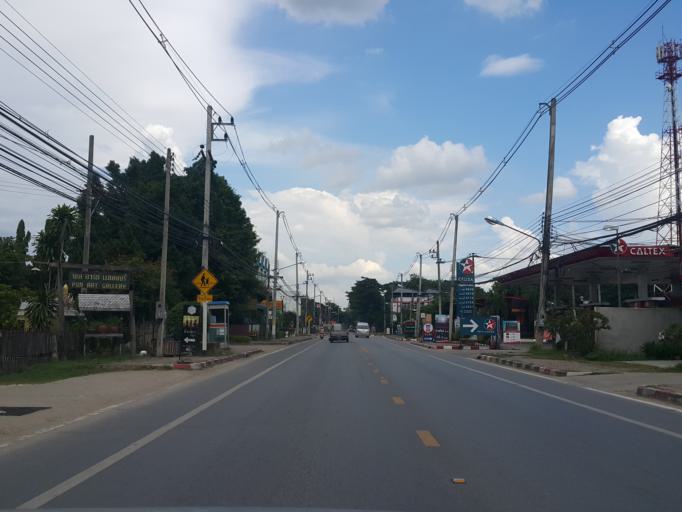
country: TH
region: Chiang Mai
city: Saraphi
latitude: 18.7777
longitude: 99.0539
